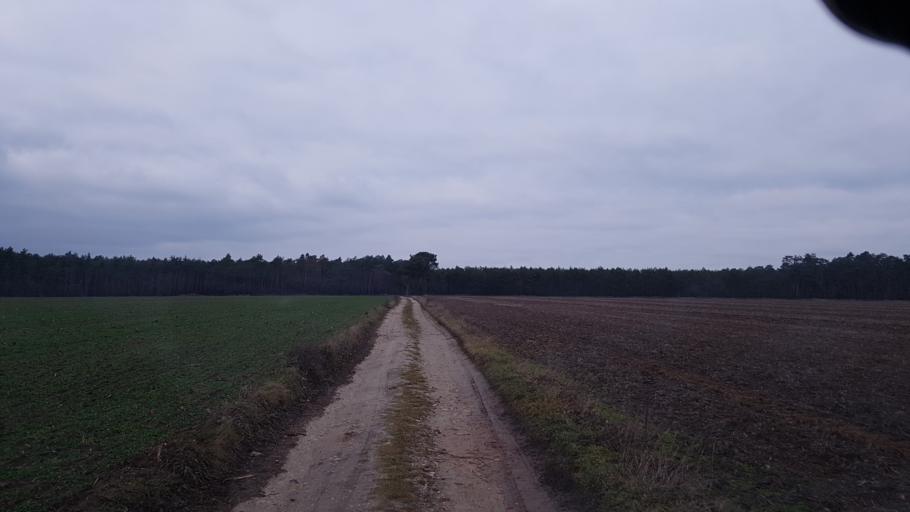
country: DE
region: Brandenburg
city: Finsterwalde
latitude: 51.6141
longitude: 13.6501
